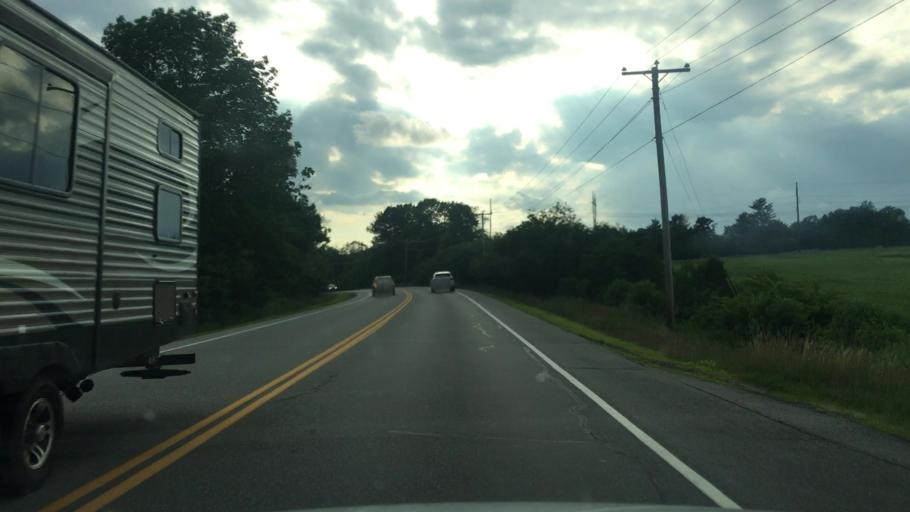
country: US
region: Maine
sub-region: Waldo County
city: Palermo
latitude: 44.4102
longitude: -69.5249
